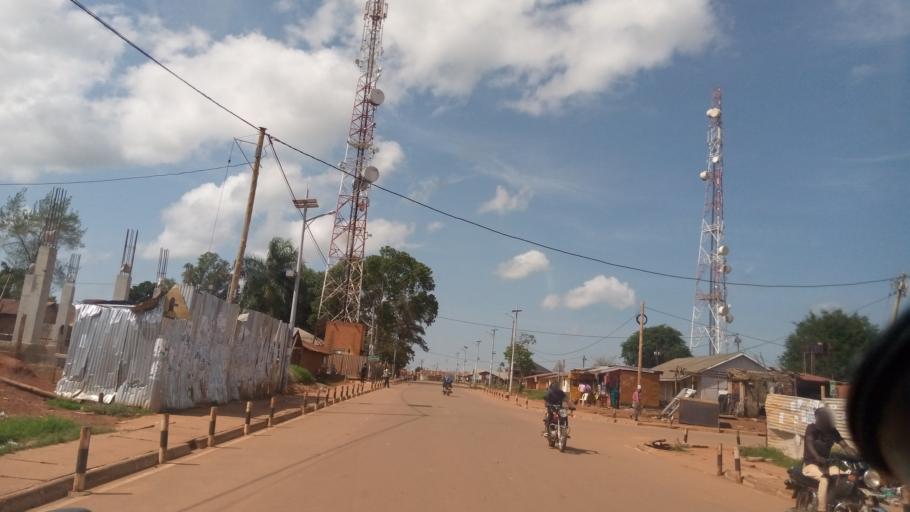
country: UG
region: Northern Region
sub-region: Gulu District
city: Gulu
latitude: 2.7699
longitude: 32.3018
